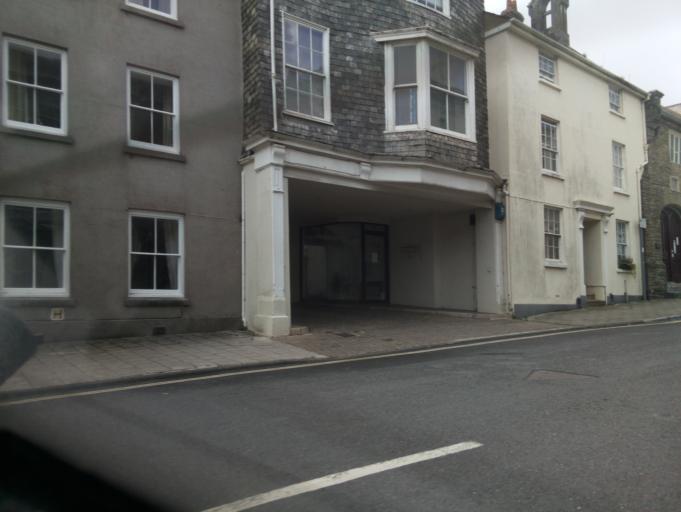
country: GB
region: England
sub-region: Devon
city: Kingsbridge
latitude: 50.2872
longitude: -3.7779
